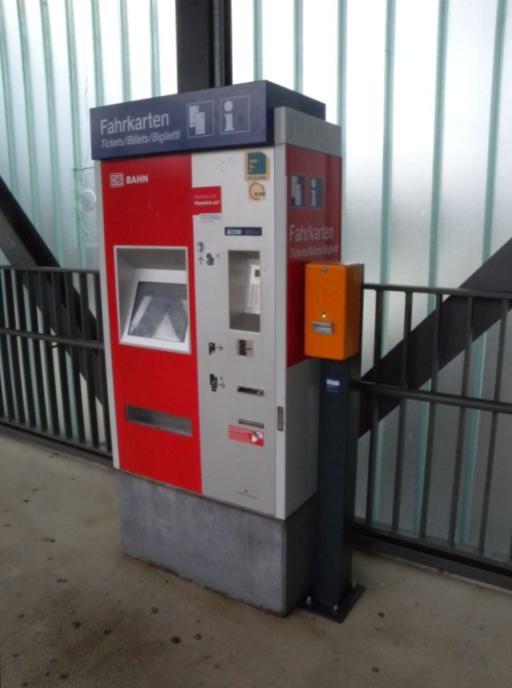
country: DE
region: Baden-Wuerttemberg
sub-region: Regierungsbezirk Stuttgart
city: Goeppingen
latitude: 48.6997
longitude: 9.6527
